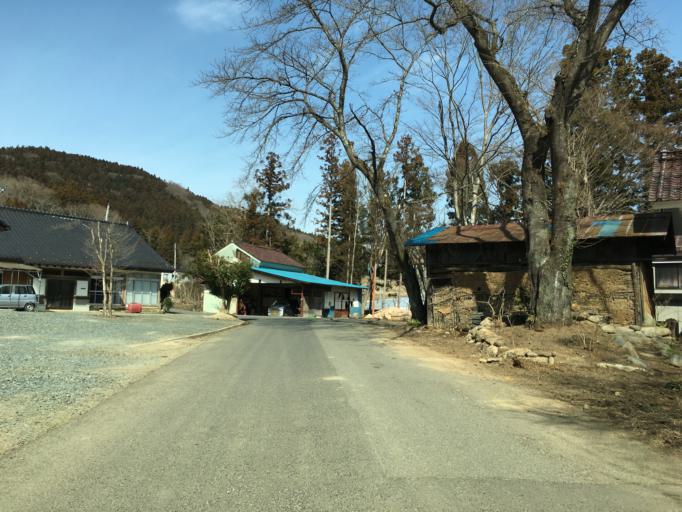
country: JP
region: Fukushima
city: Nihommatsu
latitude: 37.5974
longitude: 140.3834
